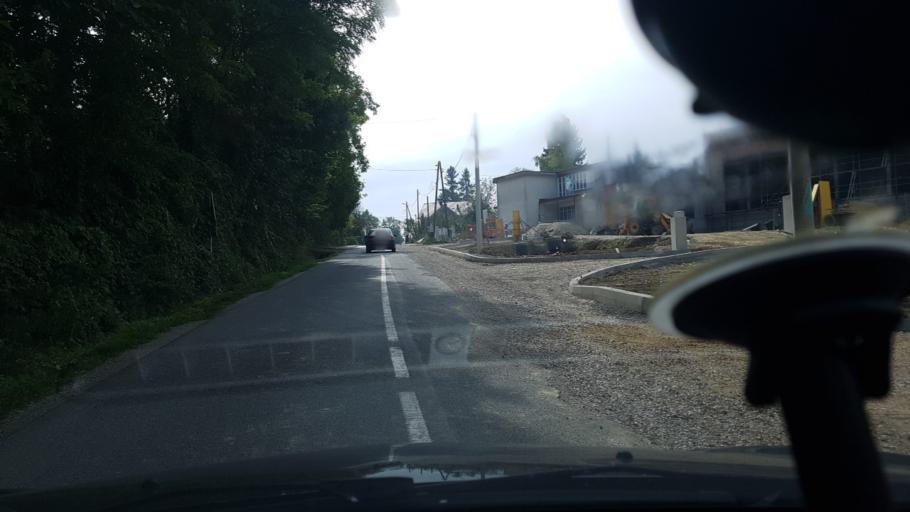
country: HR
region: Varazdinska
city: Remetinec
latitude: 46.1092
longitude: 16.2165
